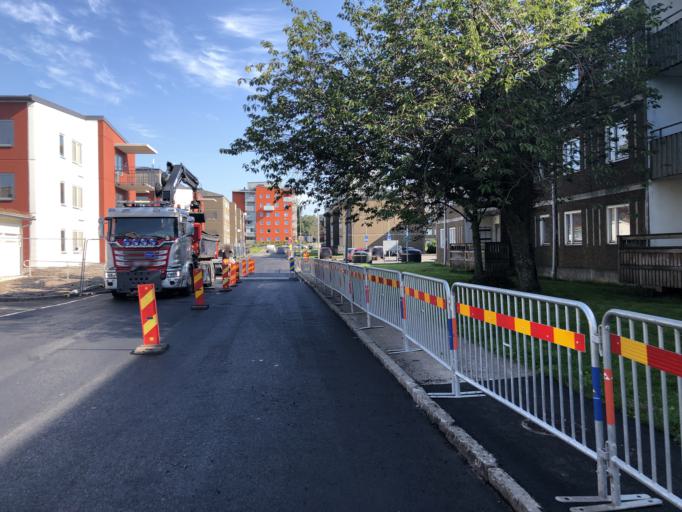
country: SE
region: Vaestra Goetaland
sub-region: Goteborg
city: Goeteborg
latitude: 57.7419
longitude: 11.9686
